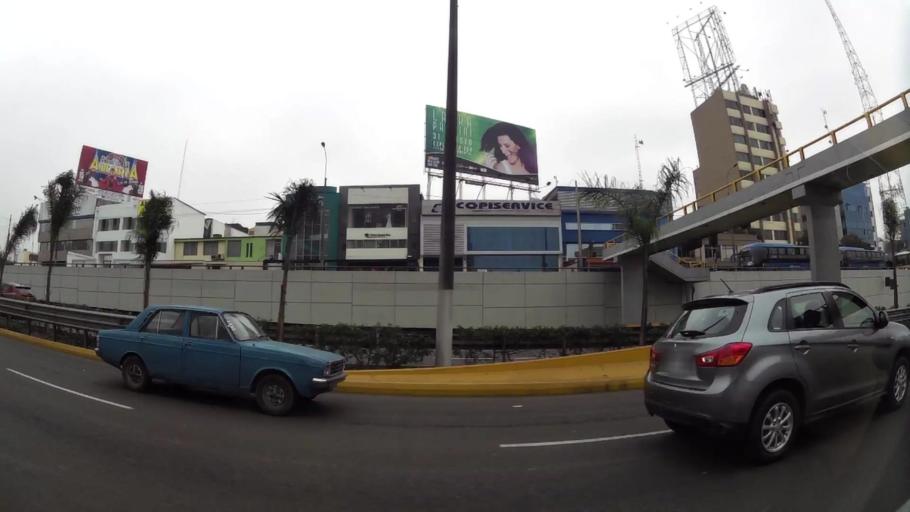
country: PE
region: Lima
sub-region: Lima
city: San Luis
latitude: -12.0879
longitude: -77.0009
